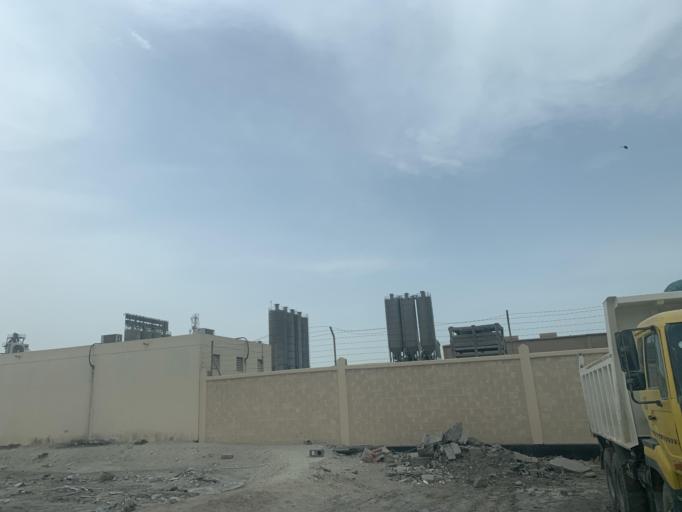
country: BH
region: Muharraq
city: Al Hadd
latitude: 26.2080
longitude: 50.6636
